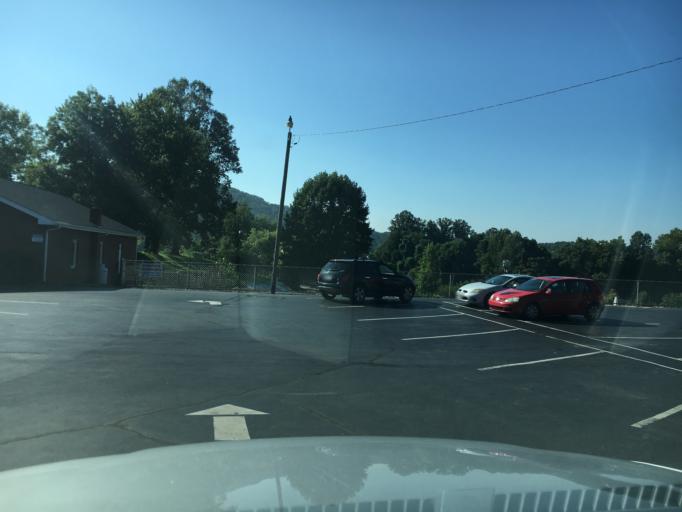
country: US
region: North Carolina
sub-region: McDowell County
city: Marion
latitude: 35.6818
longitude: -82.0150
